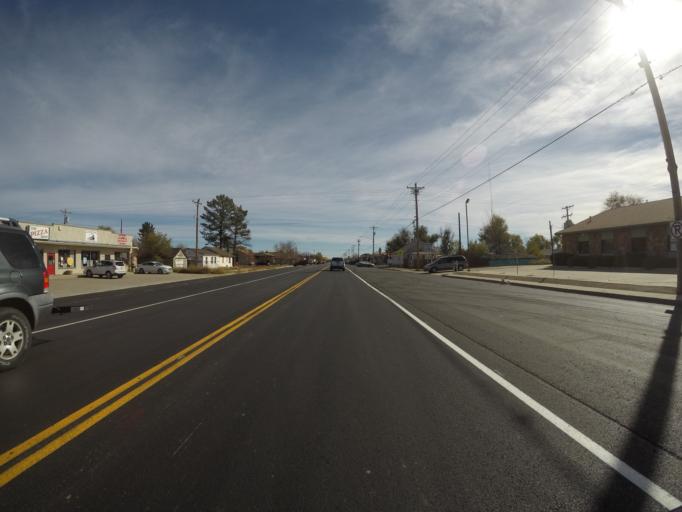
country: US
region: Colorado
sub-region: Adams County
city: Strasburg
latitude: 39.7383
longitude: -104.3260
